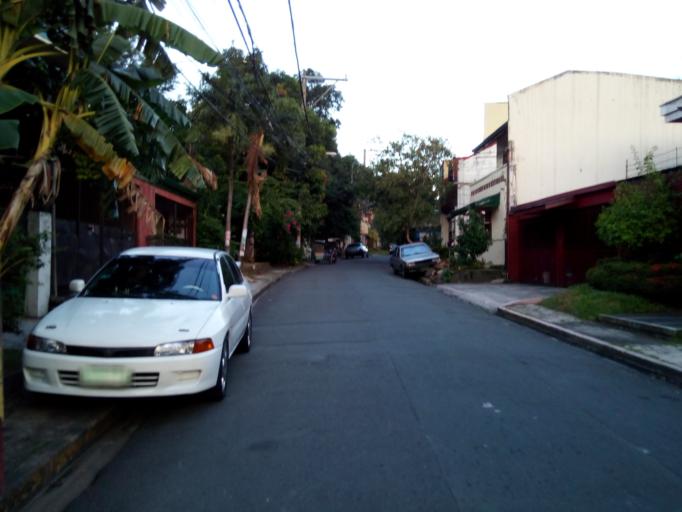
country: PH
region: Metro Manila
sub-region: Quezon City
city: Quezon City
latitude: 14.6462
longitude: 121.0573
